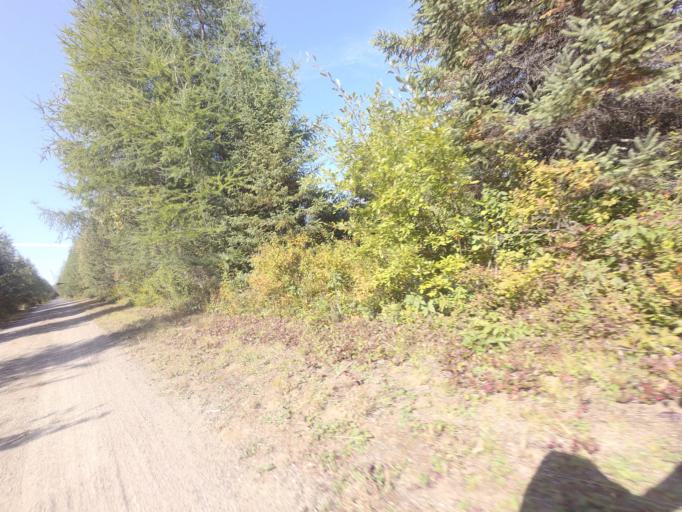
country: CA
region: Quebec
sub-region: Laurentides
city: Sainte-Agathe-des-Monts
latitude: 46.1033
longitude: -74.3720
